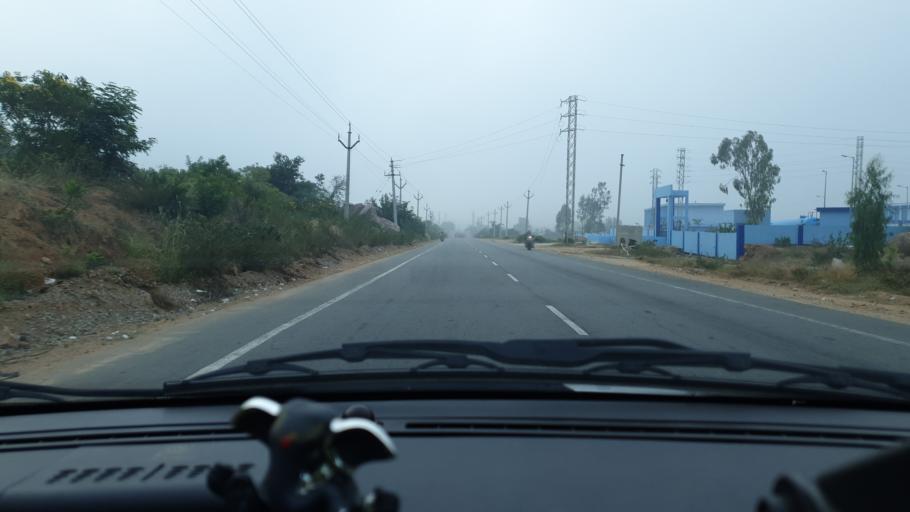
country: IN
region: Telangana
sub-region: Mahbubnagar
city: Farrukhnagar
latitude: 16.9071
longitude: 78.5290
